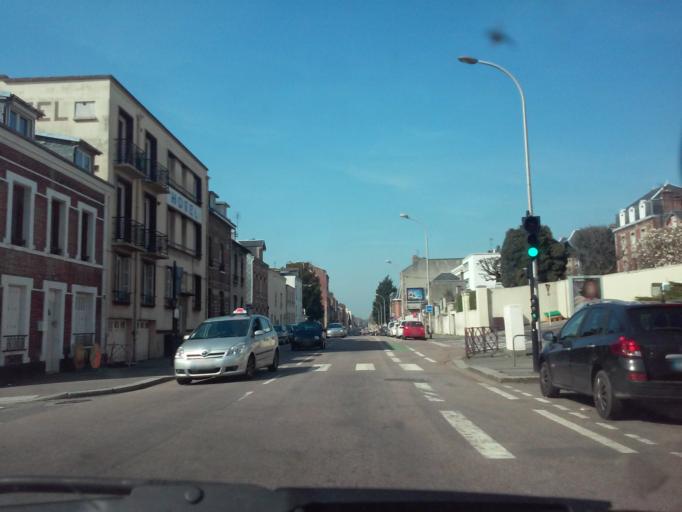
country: FR
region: Haute-Normandie
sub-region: Departement de la Seine-Maritime
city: Fontaine-la-Mallet
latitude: 49.5022
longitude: 0.1578
